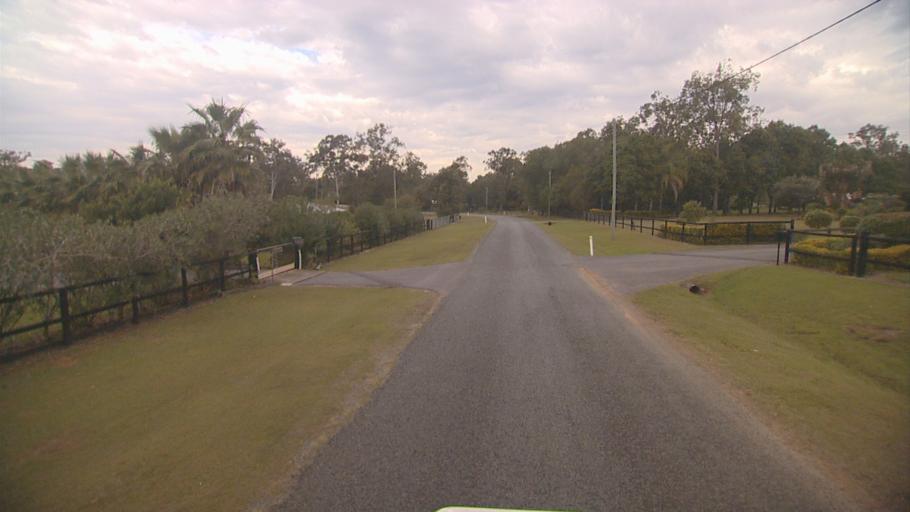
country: AU
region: Queensland
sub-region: Logan
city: Chambers Flat
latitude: -27.7925
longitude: 153.1117
